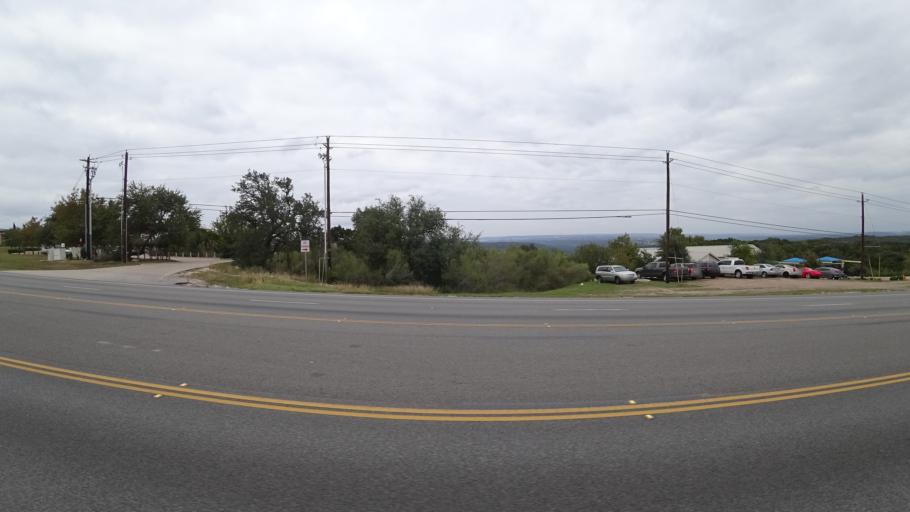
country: US
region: Texas
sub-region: Travis County
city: Bee Cave
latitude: 30.3266
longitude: -97.9636
